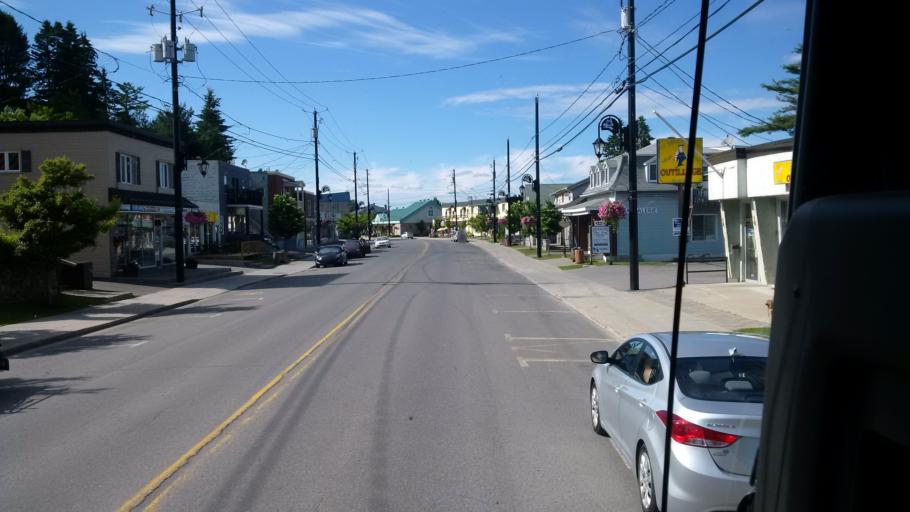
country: CA
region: Quebec
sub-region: Laurentides
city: Riviere-Rouge
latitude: 46.4125
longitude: -74.8703
